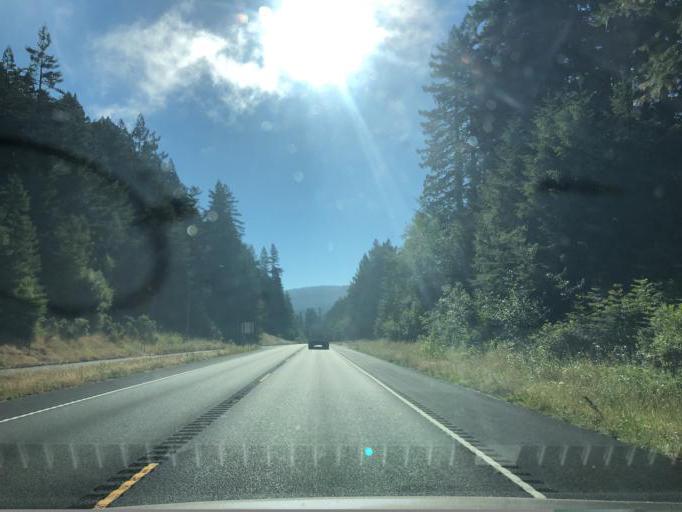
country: US
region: California
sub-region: Humboldt County
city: Blue Lake
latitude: 40.8843
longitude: -123.9623
